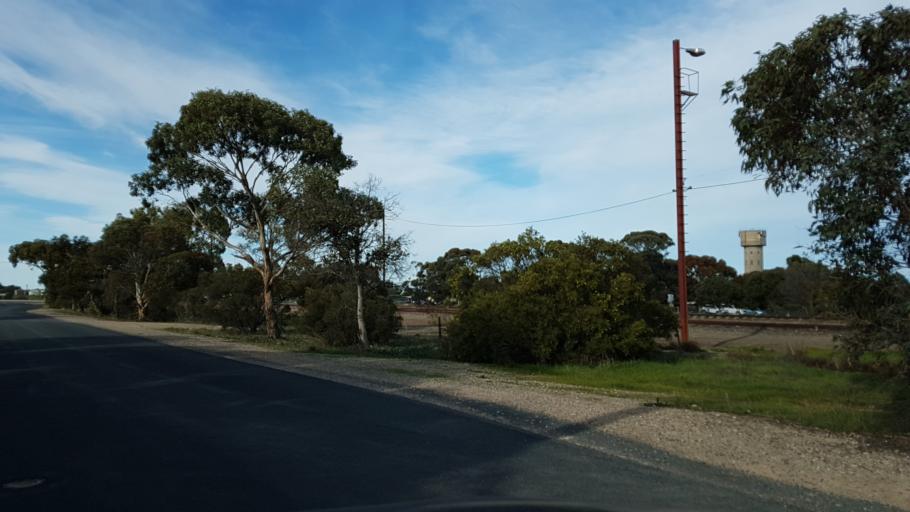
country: AU
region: South Australia
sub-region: Murray Bridge
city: Tailem Bend
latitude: -35.2510
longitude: 139.4532
